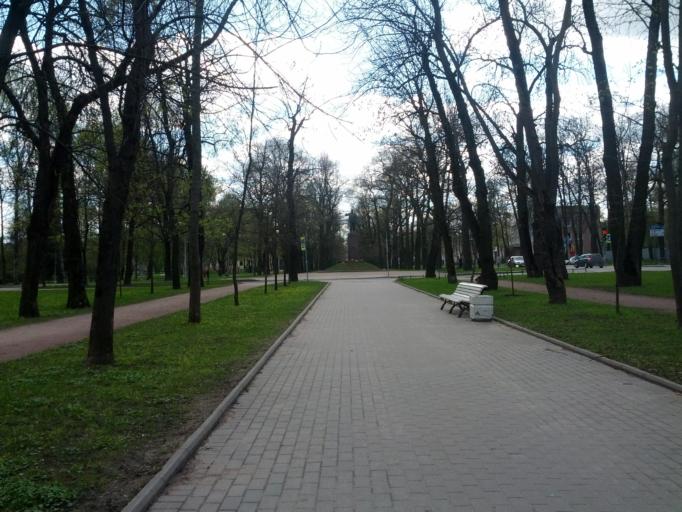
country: RU
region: St.-Petersburg
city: Pushkin
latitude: 59.7199
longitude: 30.4253
